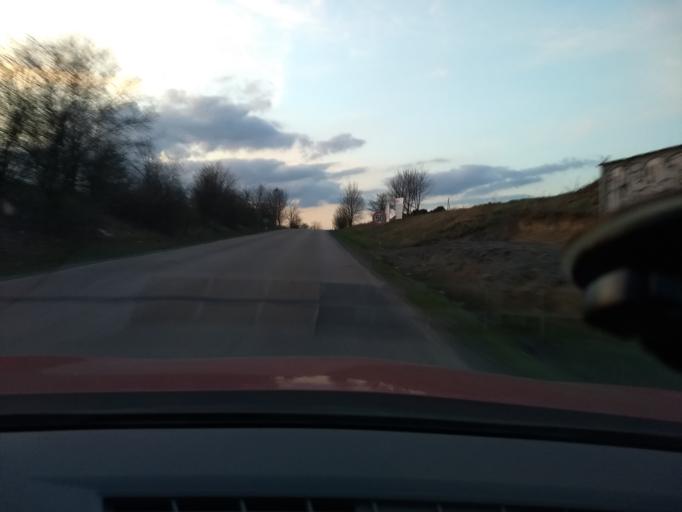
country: CZ
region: Central Bohemia
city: Rudna
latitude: 50.0486
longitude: 14.2560
